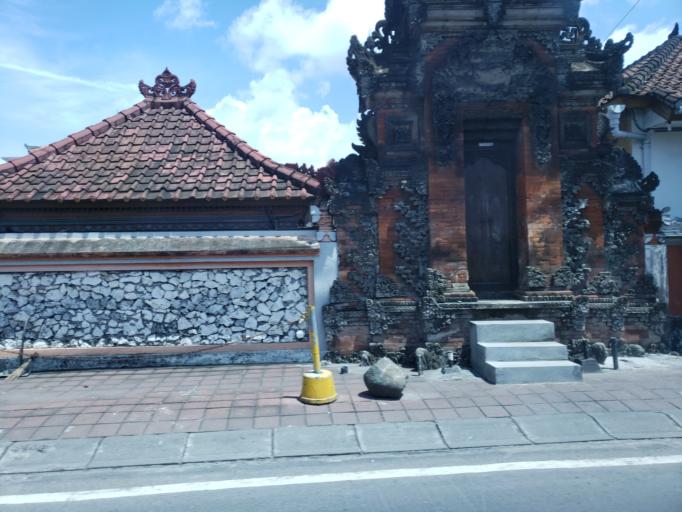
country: ID
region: Bali
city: Kelanabian
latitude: -8.7688
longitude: 115.1737
